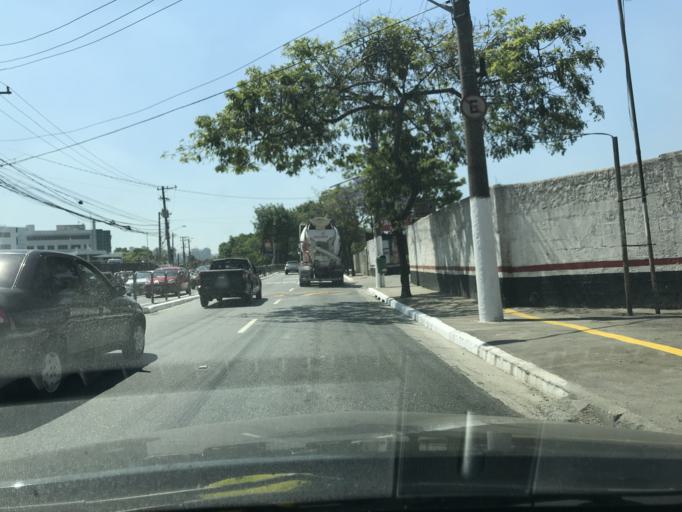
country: BR
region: Sao Paulo
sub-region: Taboao Da Serra
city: Taboao da Serra
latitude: -23.6557
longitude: -46.7242
